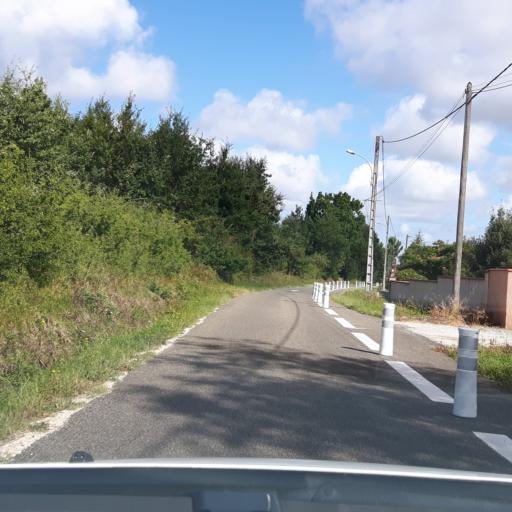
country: FR
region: Midi-Pyrenees
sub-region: Departement de la Haute-Garonne
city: Bouloc
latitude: 43.7907
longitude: 1.4079
